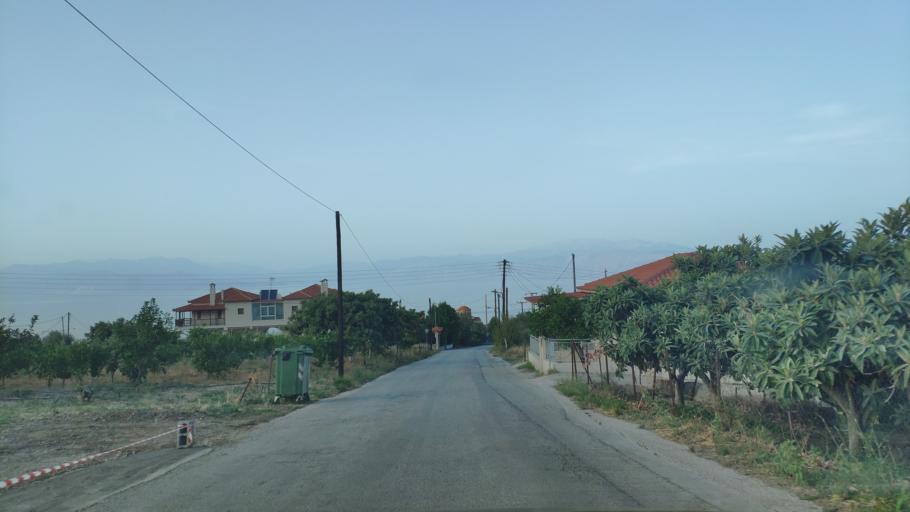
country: GR
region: West Greece
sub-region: Nomos Achaias
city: Aiyira
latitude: 38.1265
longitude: 22.3994
